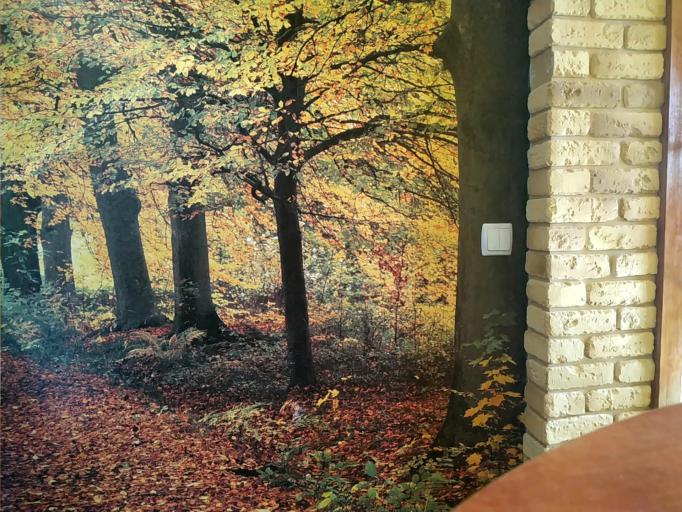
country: RU
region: Jaroslavl
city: Kukoboy
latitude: 58.8567
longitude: 39.7324
